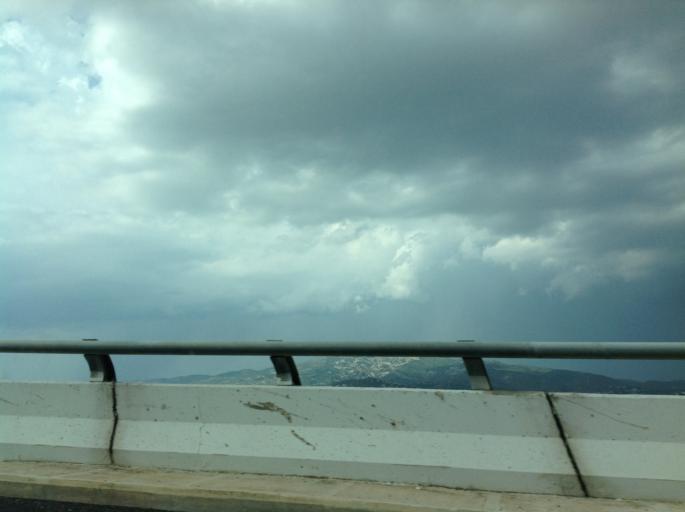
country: GR
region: Attica
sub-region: Nomarchia Athinas
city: Agia Paraskevi
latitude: 38.0091
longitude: 23.8425
